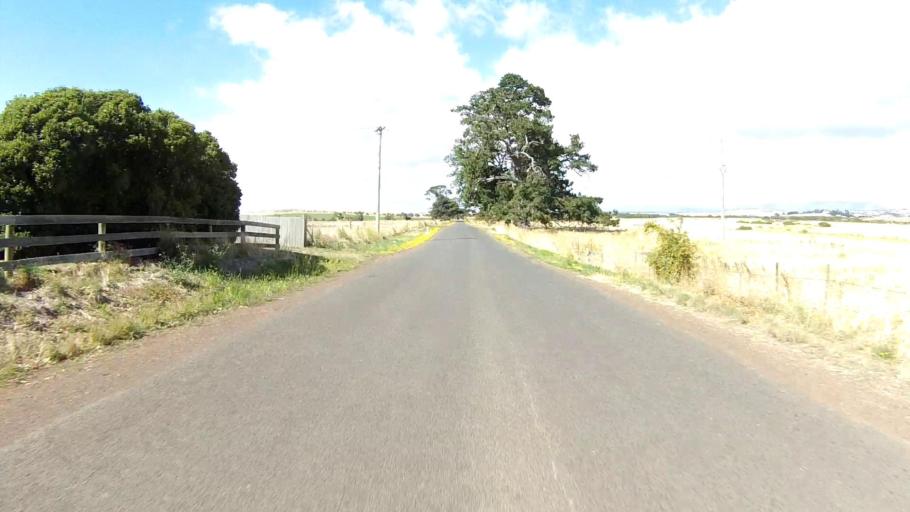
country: AU
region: Tasmania
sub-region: Northern Midlands
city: Evandale
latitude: -41.7535
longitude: 147.4874
